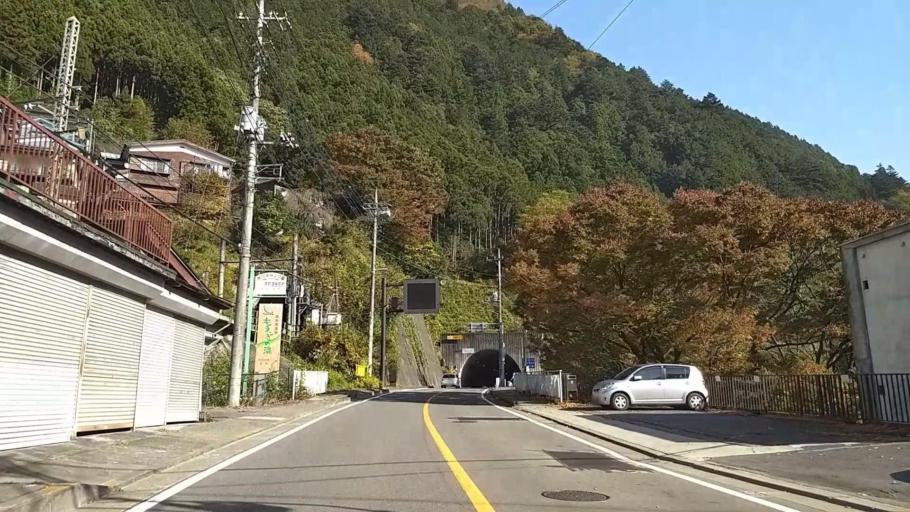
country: JP
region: Tokyo
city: Itsukaichi
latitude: 35.8083
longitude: 139.0990
